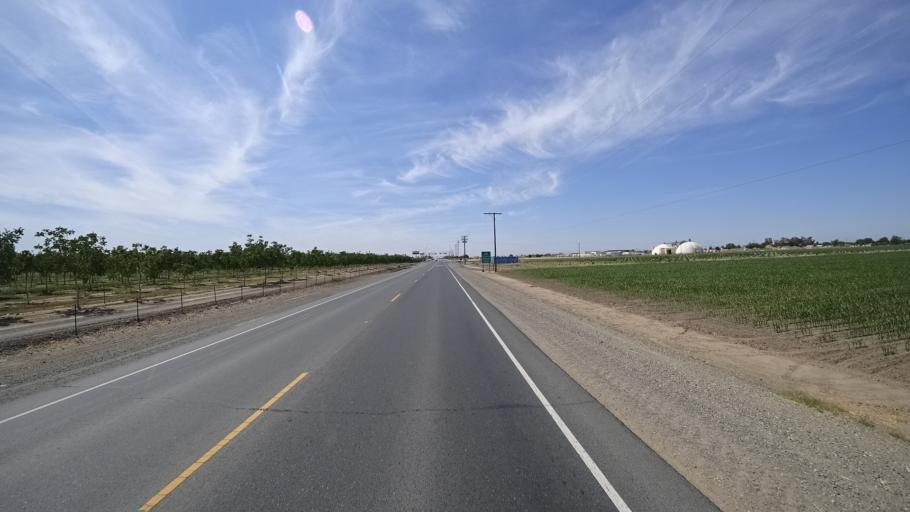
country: US
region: California
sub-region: Kings County
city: Hanford
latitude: 36.3343
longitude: -119.6010
